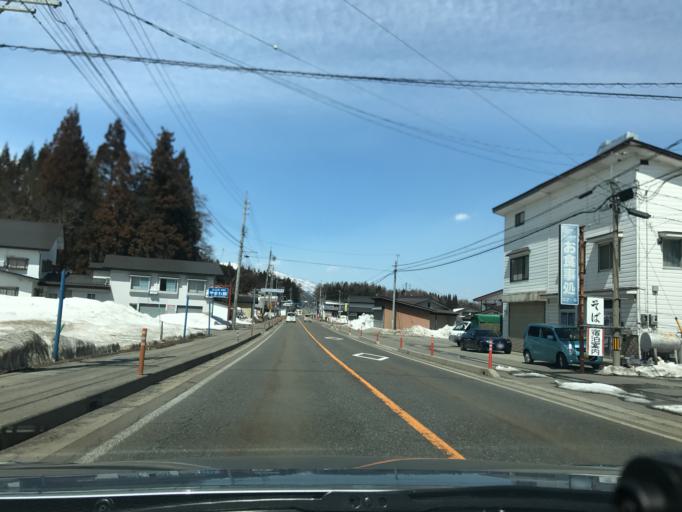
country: JP
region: Nagano
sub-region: Kitaazumi Gun
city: Hakuba
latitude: 36.6332
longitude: 137.8447
